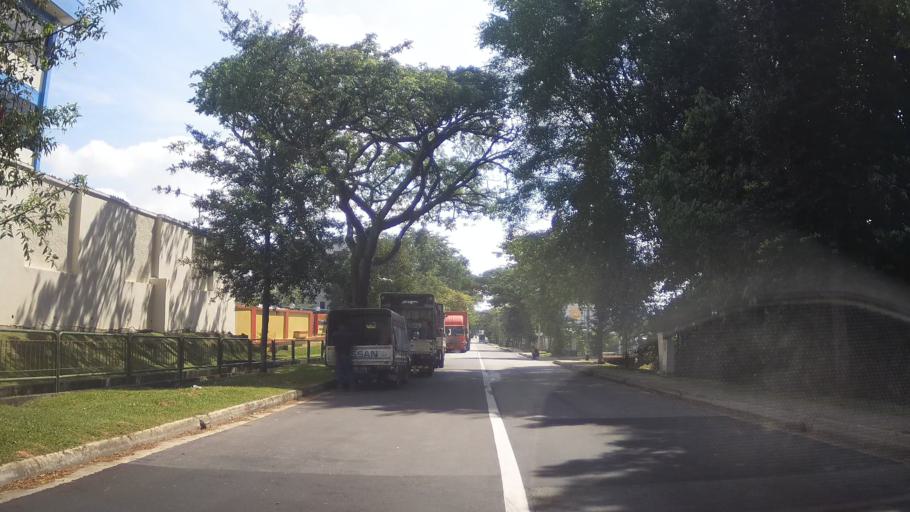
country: SG
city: Singapore
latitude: 1.3198
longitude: 103.7114
